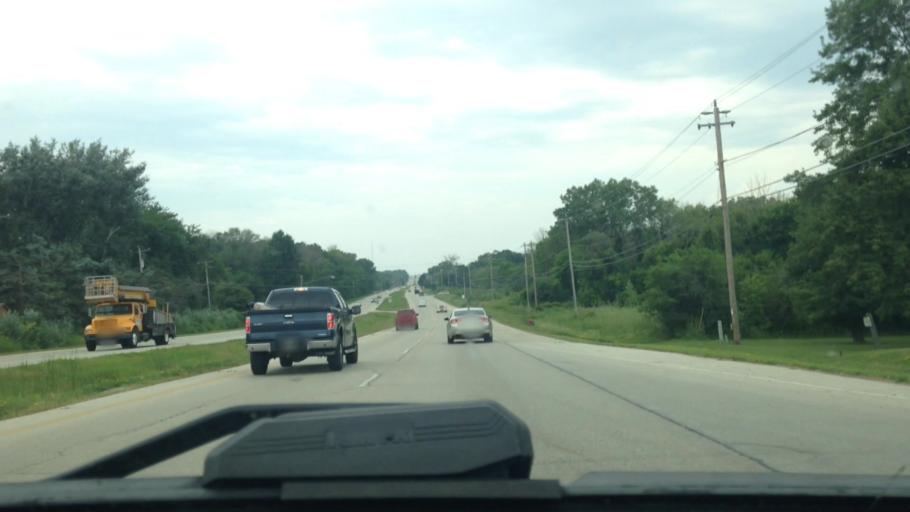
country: US
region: Wisconsin
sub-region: Waukesha County
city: Butler
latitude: 43.1193
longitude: -88.0884
